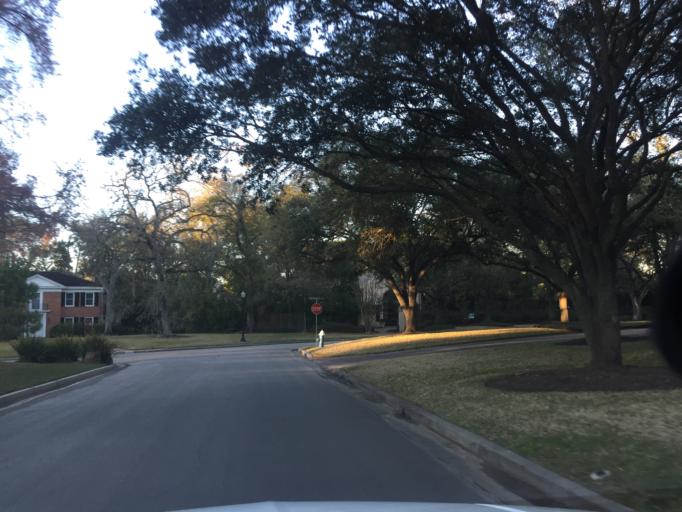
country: US
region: Texas
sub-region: Harris County
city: West University Place
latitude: 29.7530
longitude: -95.4376
